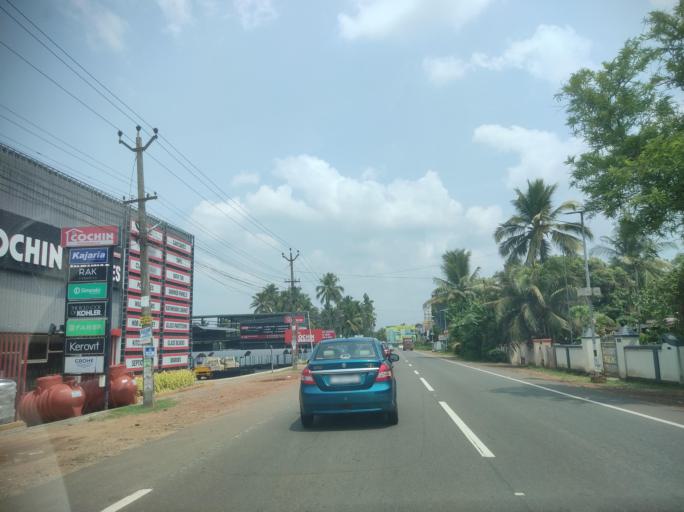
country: IN
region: Kerala
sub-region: Kottayam
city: Changanacheri
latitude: 9.4117
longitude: 76.5538
